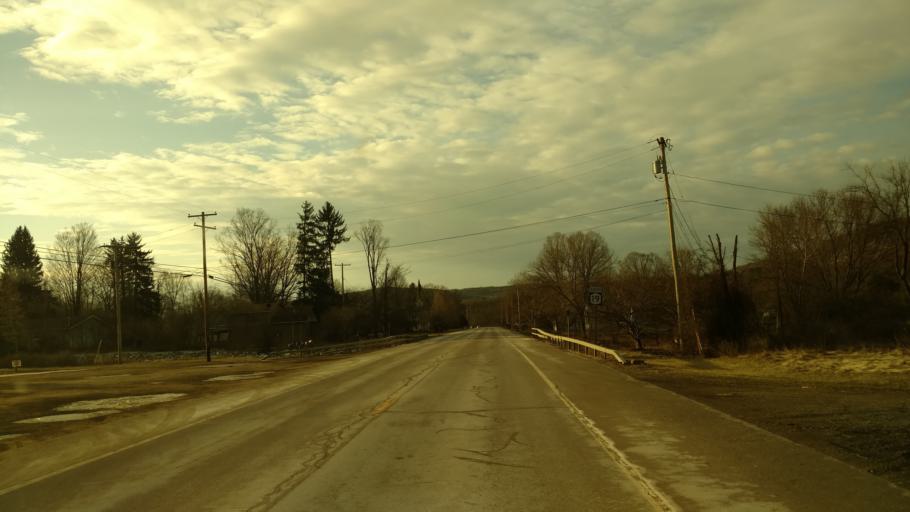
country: US
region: New York
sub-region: Allegany County
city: Wellsville
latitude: 42.0209
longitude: -77.8976
